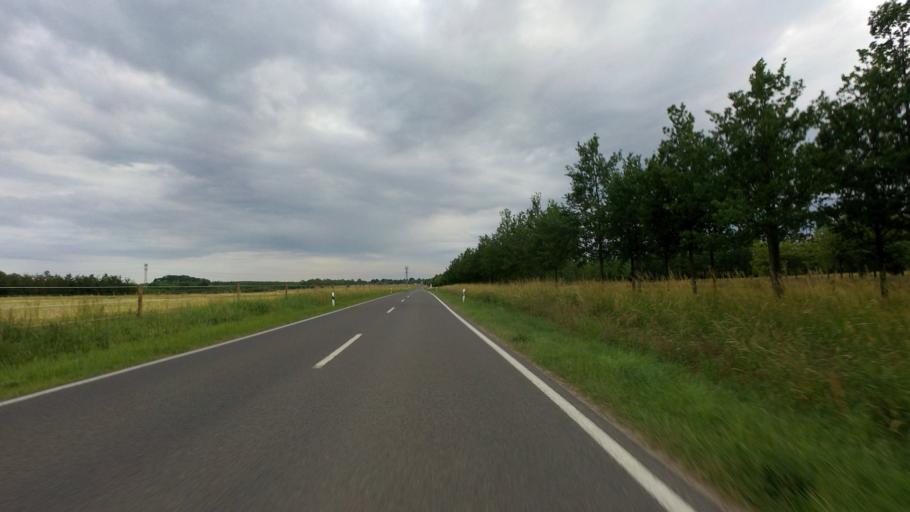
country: DE
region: Brandenburg
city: Pawesin
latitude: 52.5572
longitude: 12.7674
